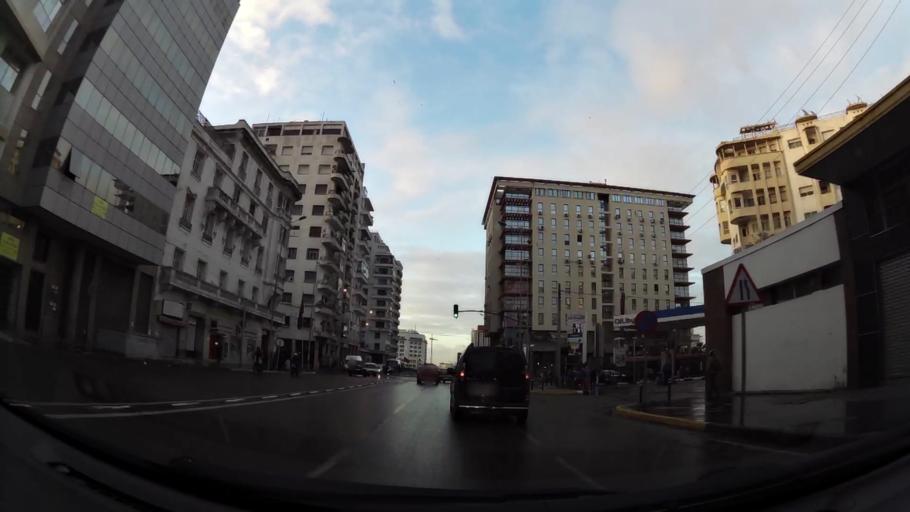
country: MA
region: Grand Casablanca
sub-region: Casablanca
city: Casablanca
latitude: 33.5930
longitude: -7.6036
